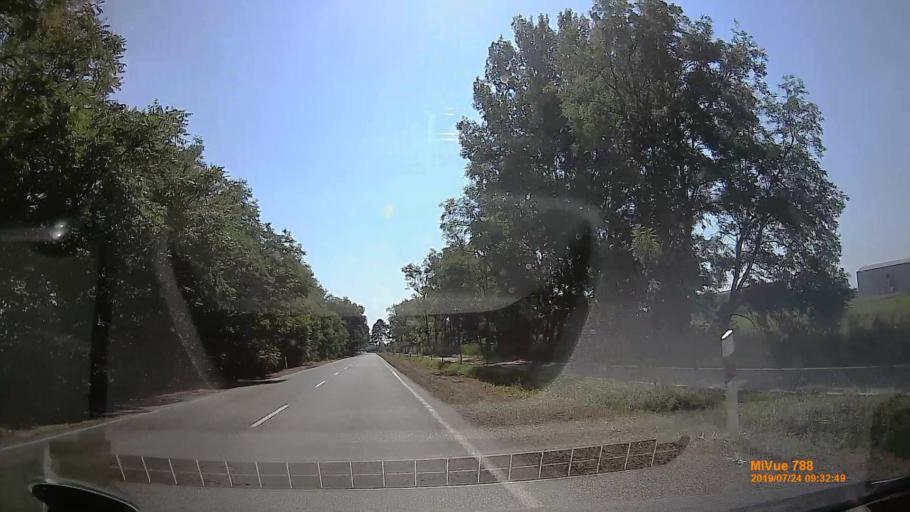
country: HU
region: Szabolcs-Szatmar-Bereg
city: Napkor
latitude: 47.9503
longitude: 21.8380
